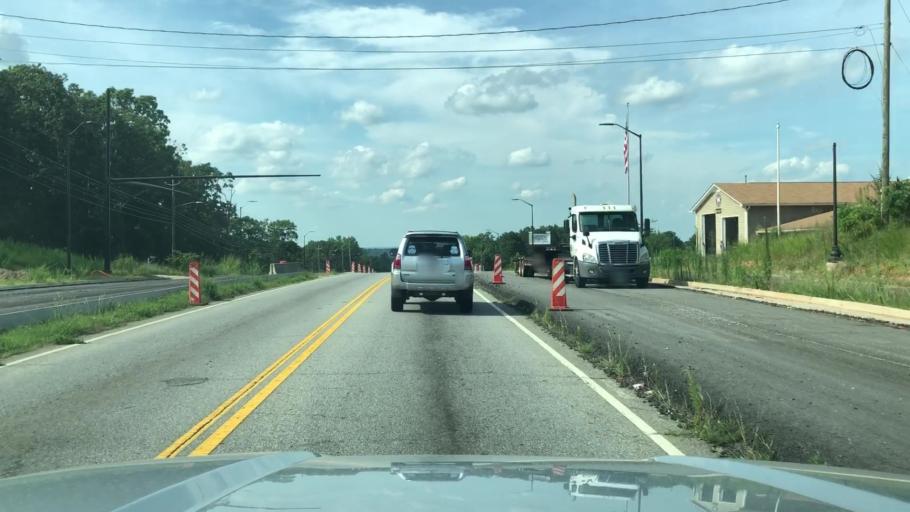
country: US
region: Georgia
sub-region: Douglas County
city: Douglasville
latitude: 33.7671
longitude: -84.7483
